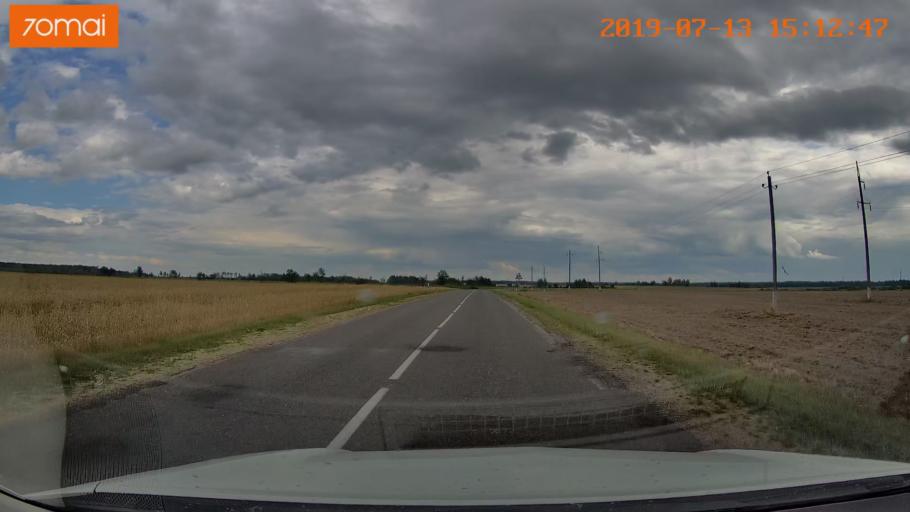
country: BY
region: Mogilev
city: Hlusha
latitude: 53.1450
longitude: 28.7976
